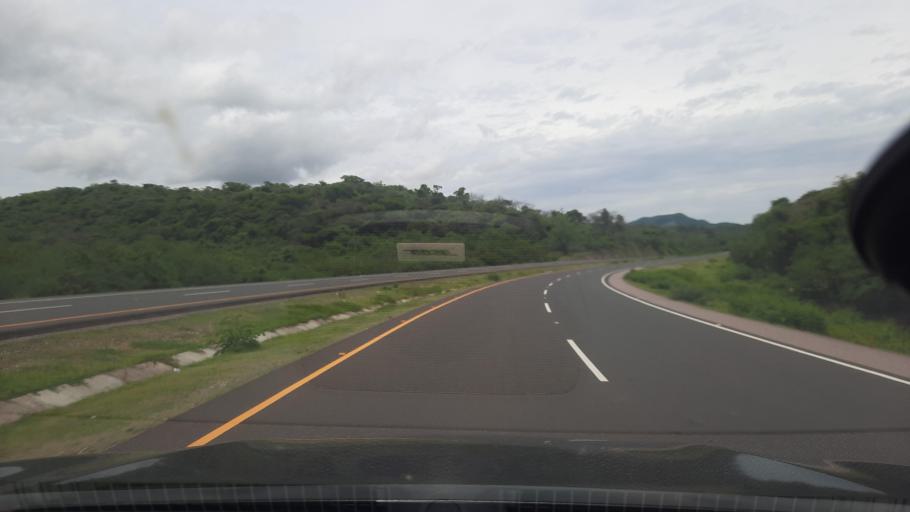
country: HN
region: Valle
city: Aramecina
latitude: 13.7140
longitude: -87.7062
